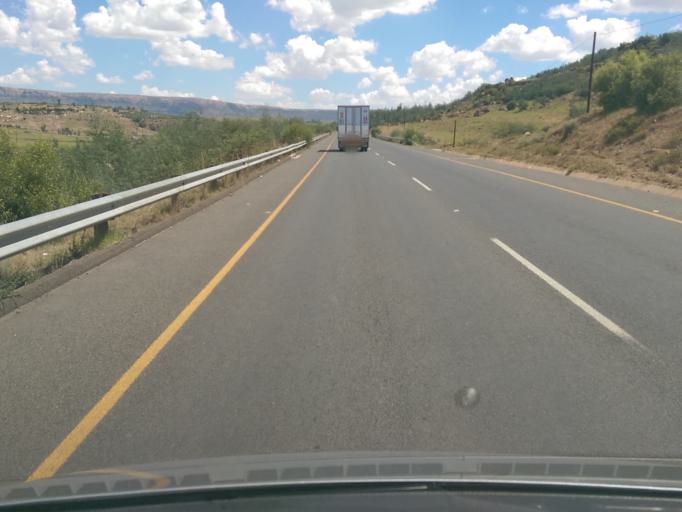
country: LS
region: Maseru
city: Maseru
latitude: -29.3963
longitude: 27.5373
